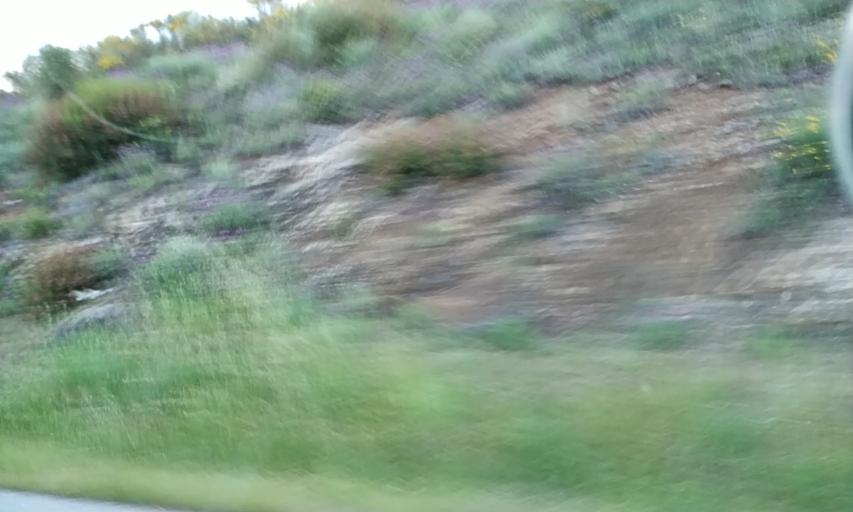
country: PT
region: Portalegre
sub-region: Portalegre
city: Sao Juliao
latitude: 39.3613
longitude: -7.3203
